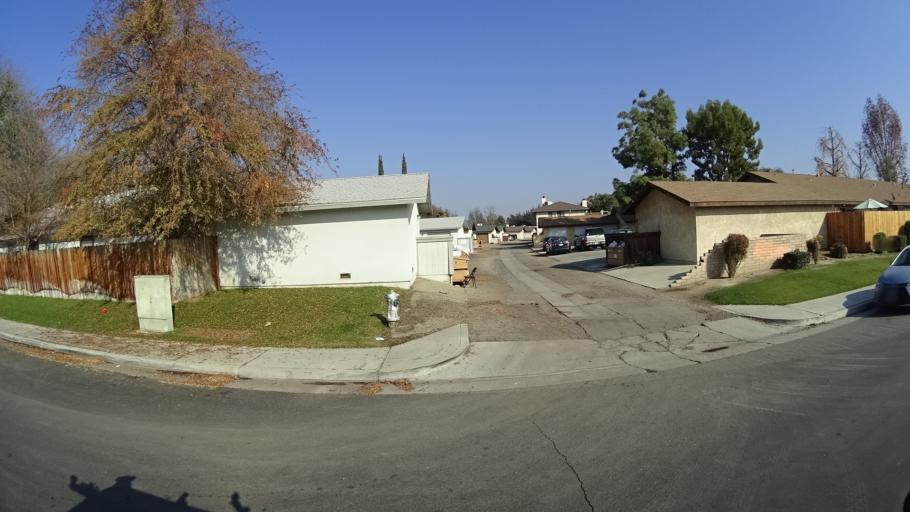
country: US
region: California
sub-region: Kern County
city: Greenacres
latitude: 35.3284
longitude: -119.0800
